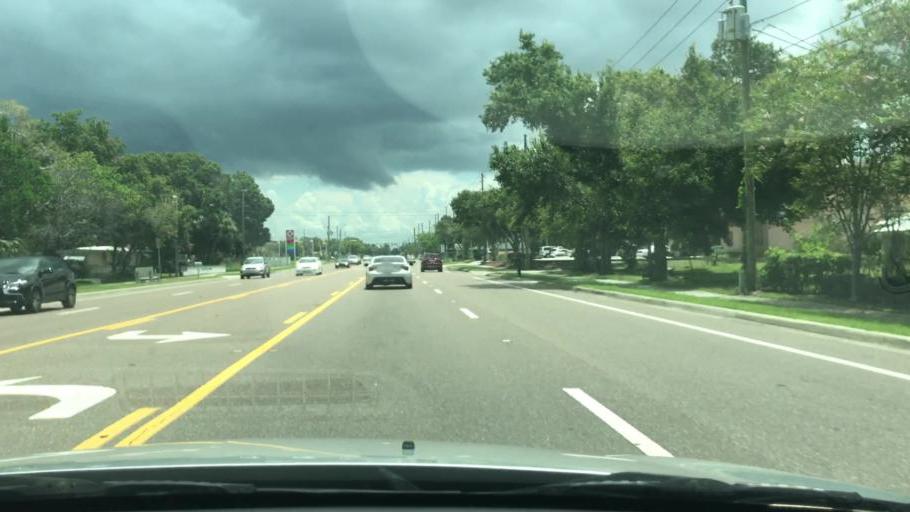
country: US
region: Florida
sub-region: Pinellas County
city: Kenneth City
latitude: 27.8209
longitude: -82.7323
